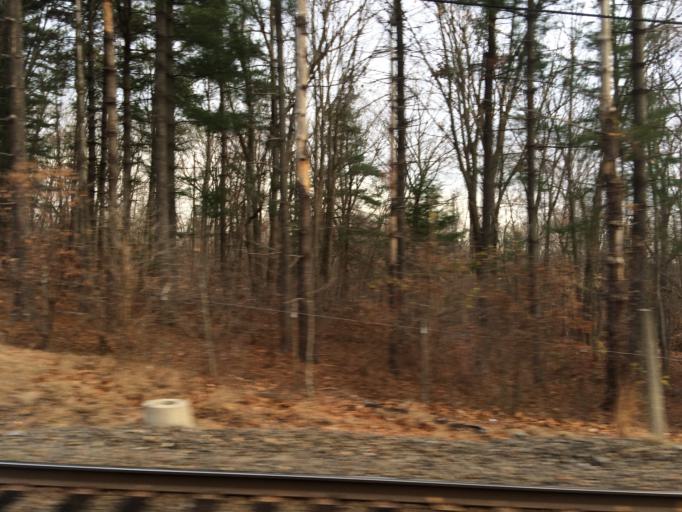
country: US
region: New Jersey
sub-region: Camden County
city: Lawnside
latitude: 39.8770
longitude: -75.0184
